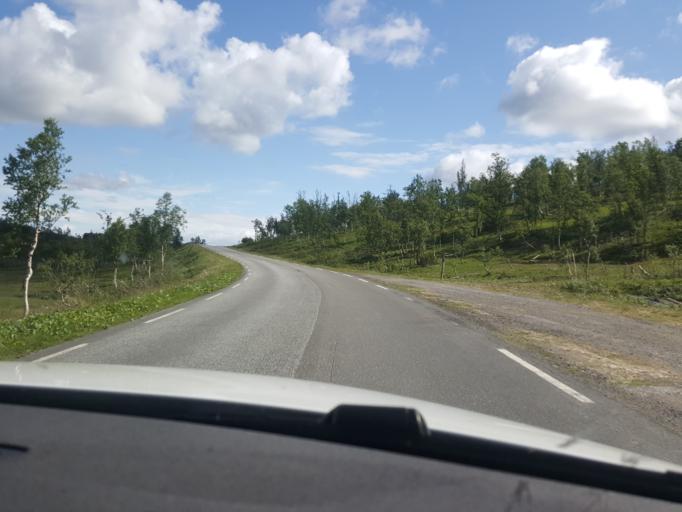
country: NO
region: Nordland
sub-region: Saltdal
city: Rognan
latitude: 67.0344
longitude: 15.1917
